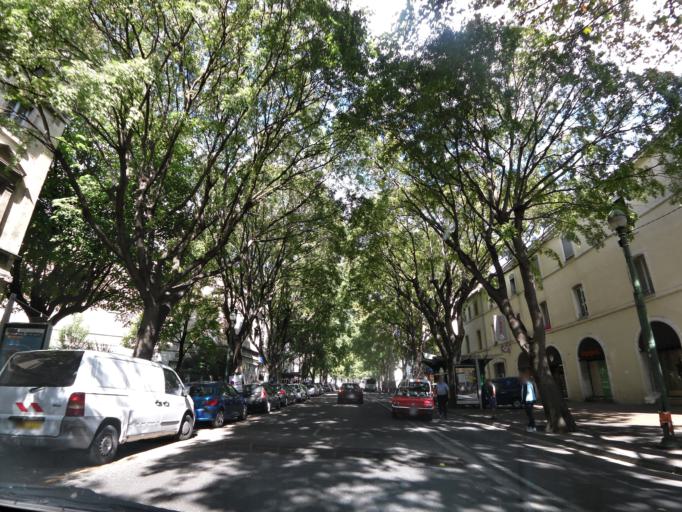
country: FR
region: Languedoc-Roussillon
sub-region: Departement du Gard
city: Nimes
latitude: 43.8374
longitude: 4.3628
